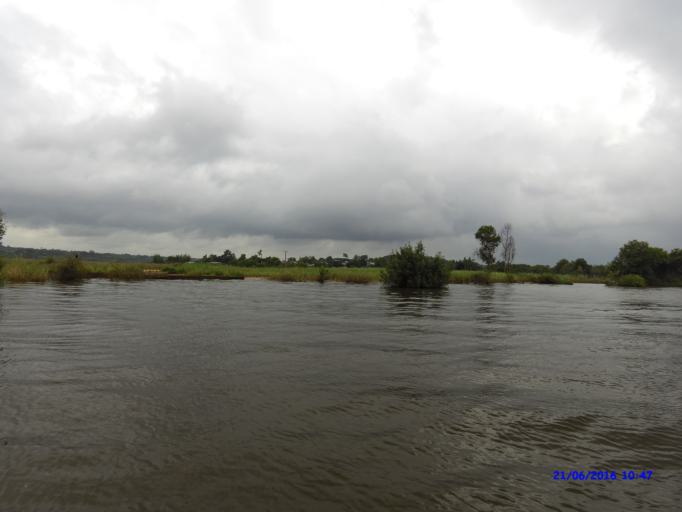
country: BJ
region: Mono
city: Come
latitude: 6.4954
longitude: 1.9579
